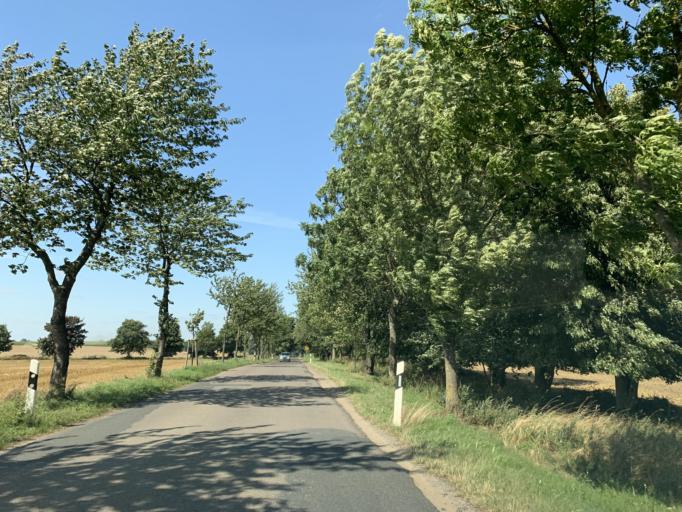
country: DE
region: Mecklenburg-Vorpommern
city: Loitz
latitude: 53.3534
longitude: 13.3910
